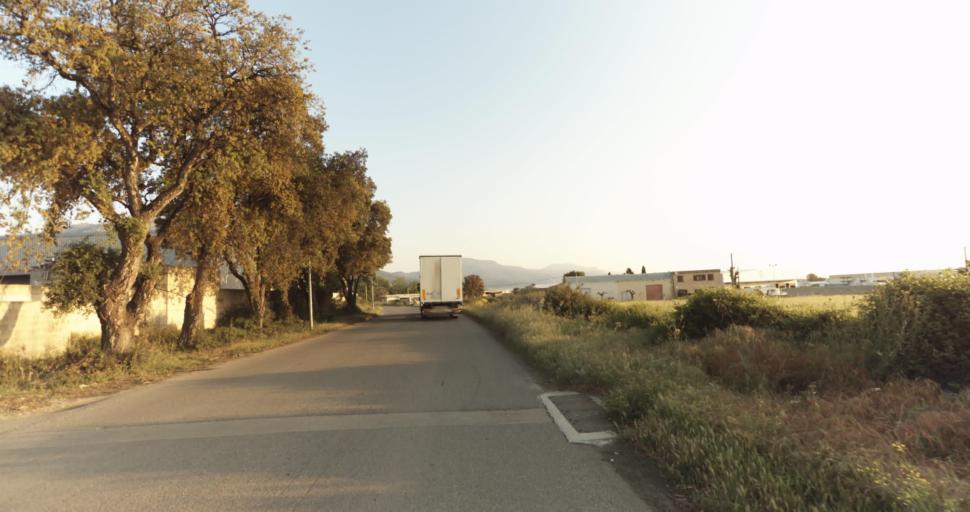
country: FR
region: Corsica
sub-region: Departement de la Haute-Corse
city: Biguglia
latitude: 42.5959
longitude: 9.4421
